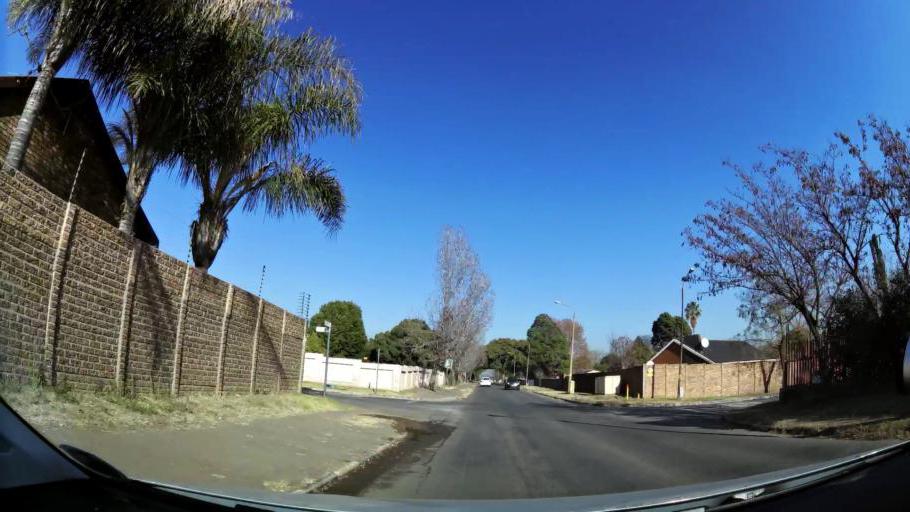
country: ZA
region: Gauteng
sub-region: City of Johannesburg Metropolitan Municipality
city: Modderfontein
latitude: -26.1336
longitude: 28.1453
